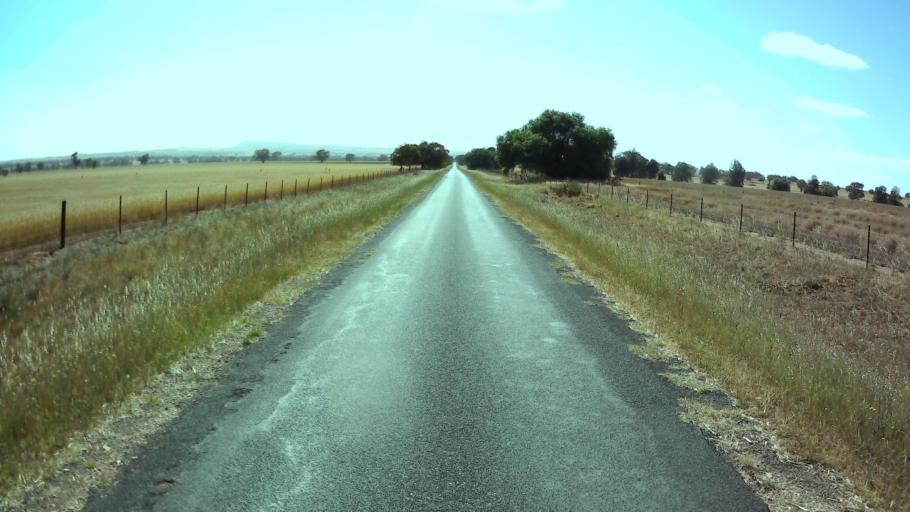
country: AU
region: New South Wales
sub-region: Weddin
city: Grenfell
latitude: -34.0617
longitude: 148.2742
